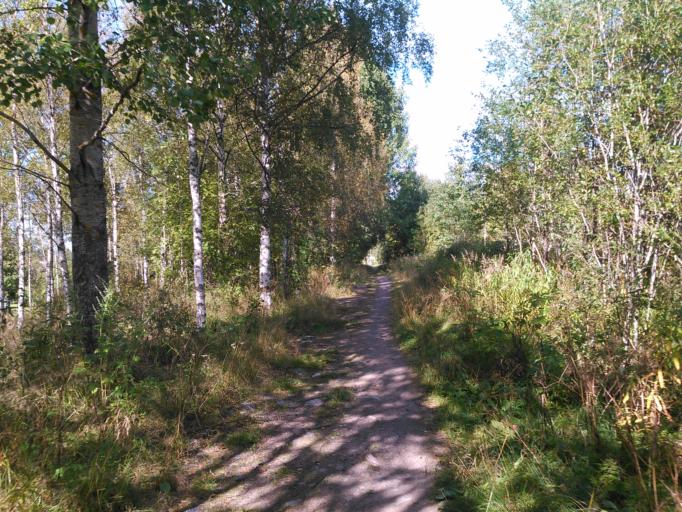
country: SE
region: Vaesterbotten
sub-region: Umea Kommun
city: Umea
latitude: 63.7949
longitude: 20.3162
